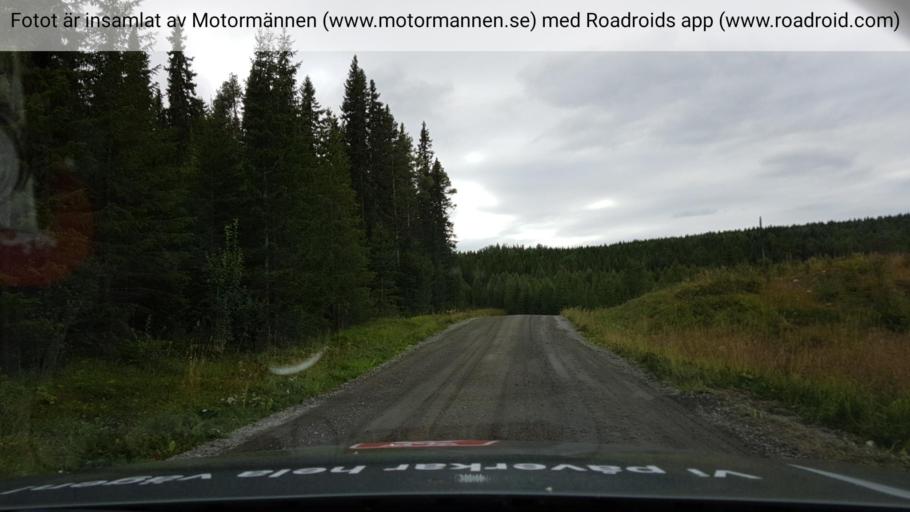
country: SE
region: Jaemtland
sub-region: Krokoms Kommun
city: Valla
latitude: 63.3970
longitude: 14.0704
